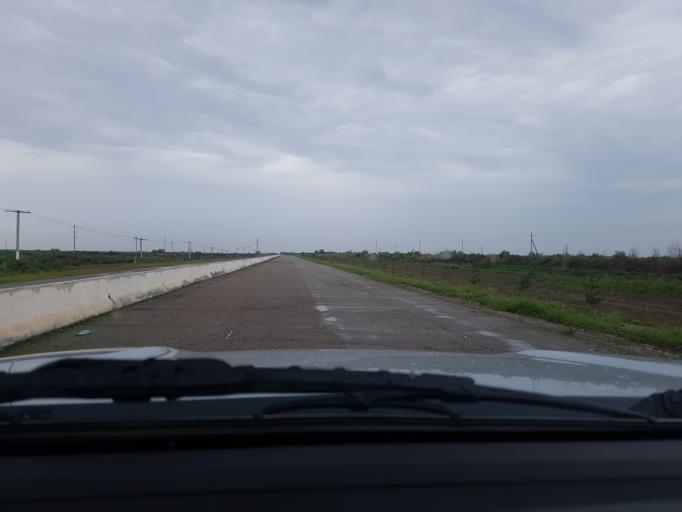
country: UZ
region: Bukhara
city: Olot
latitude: 39.2818
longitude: 63.7453
